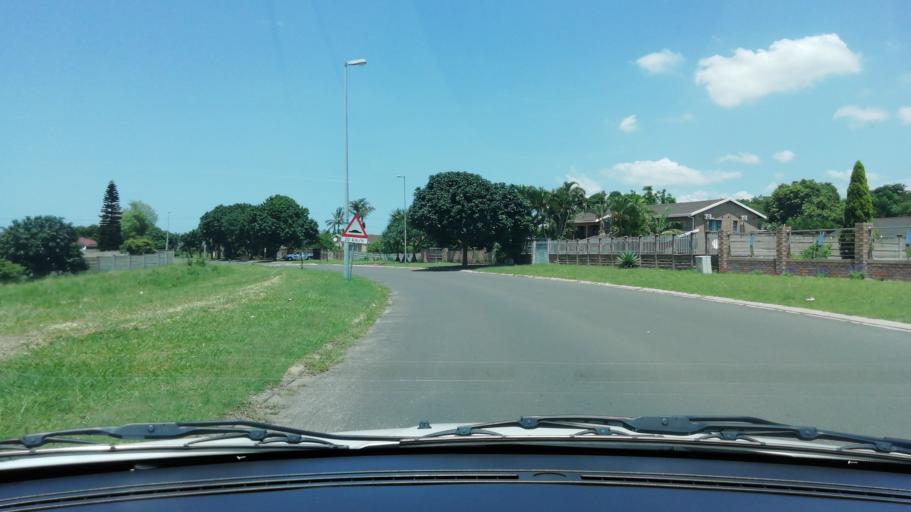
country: ZA
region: KwaZulu-Natal
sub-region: uThungulu District Municipality
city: Richards Bay
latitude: -28.7333
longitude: 32.0463
